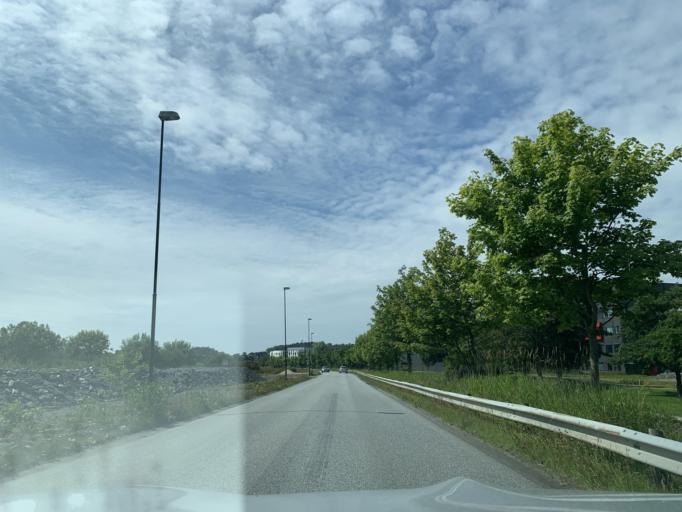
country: NO
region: Rogaland
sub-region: Sola
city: Sola
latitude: 58.8944
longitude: 5.6895
